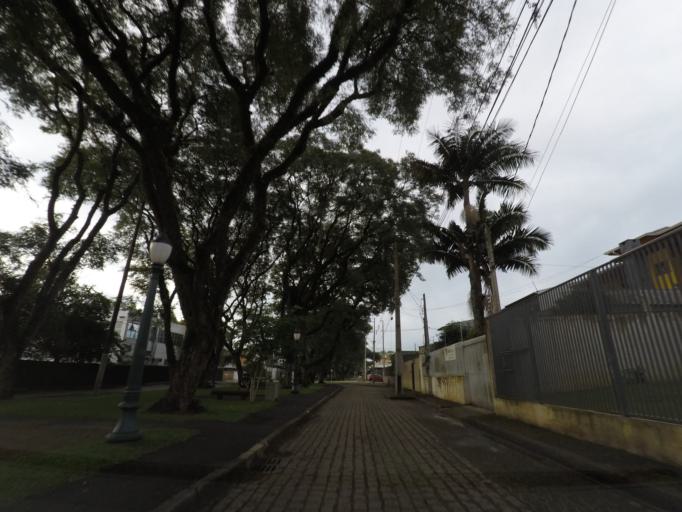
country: BR
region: Parana
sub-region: Curitiba
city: Curitiba
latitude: -25.4218
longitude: -49.2495
